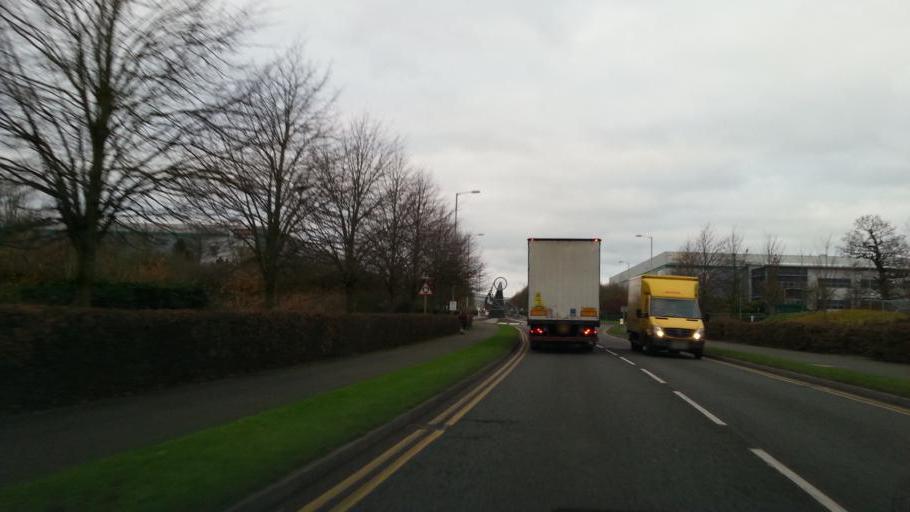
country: GB
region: England
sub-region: Coventry
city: Keresley
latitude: 52.4549
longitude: -1.5181
